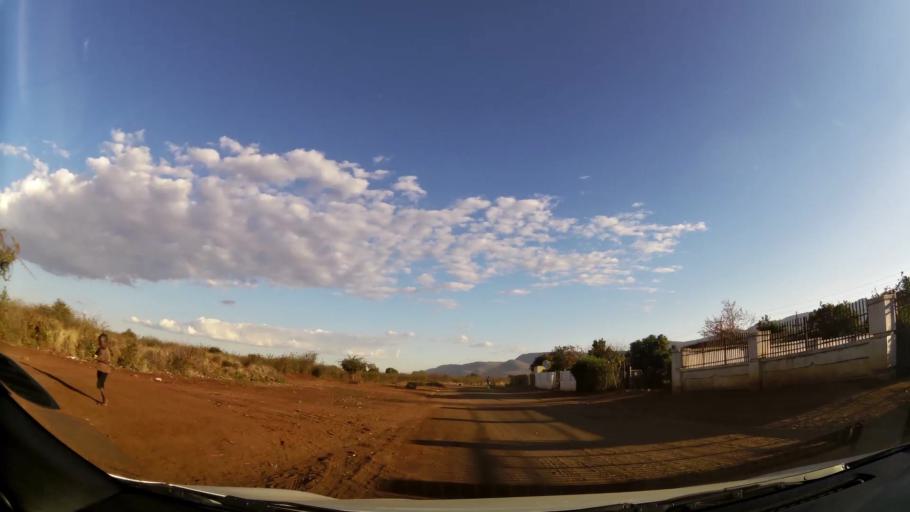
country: ZA
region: Limpopo
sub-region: Waterberg District Municipality
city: Mokopane
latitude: -24.1552
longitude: 28.9930
